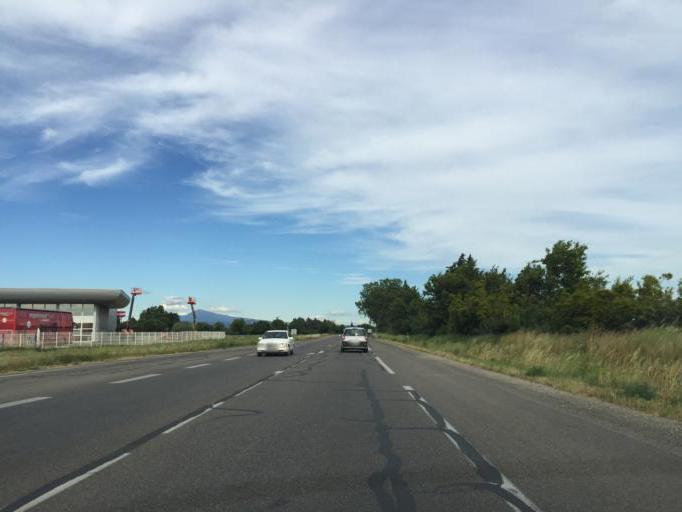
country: FR
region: Provence-Alpes-Cote d'Azur
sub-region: Departement du Vaucluse
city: Piolenc
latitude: 44.1639
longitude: 4.7788
